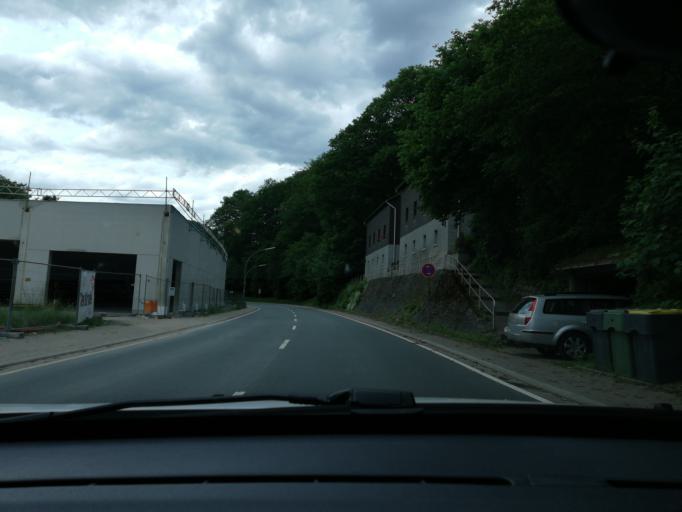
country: DE
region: North Rhine-Westphalia
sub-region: Regierungsbezirk Arnsberg
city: Schalksmuhle
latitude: 51.2489
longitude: 7.5189
